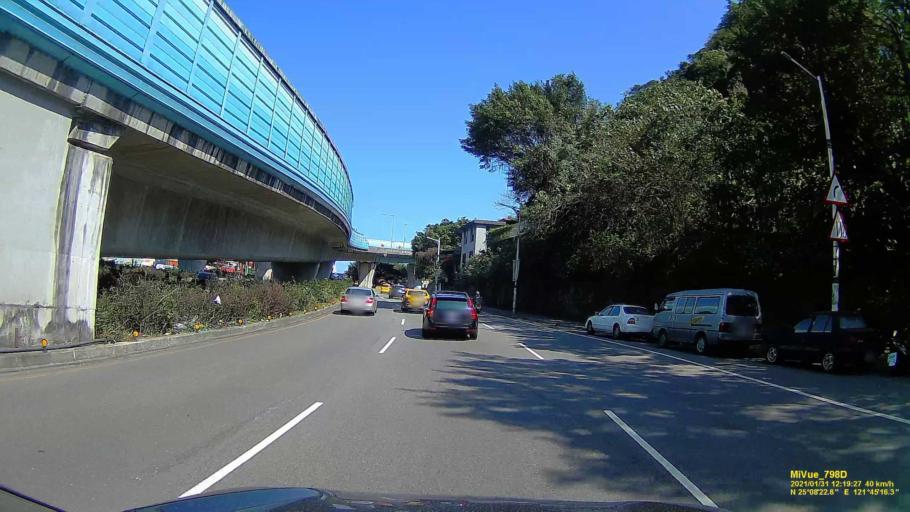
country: TW
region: Taiwan
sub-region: Keelung
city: Keelung
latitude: 25.1397
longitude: 121.7548
